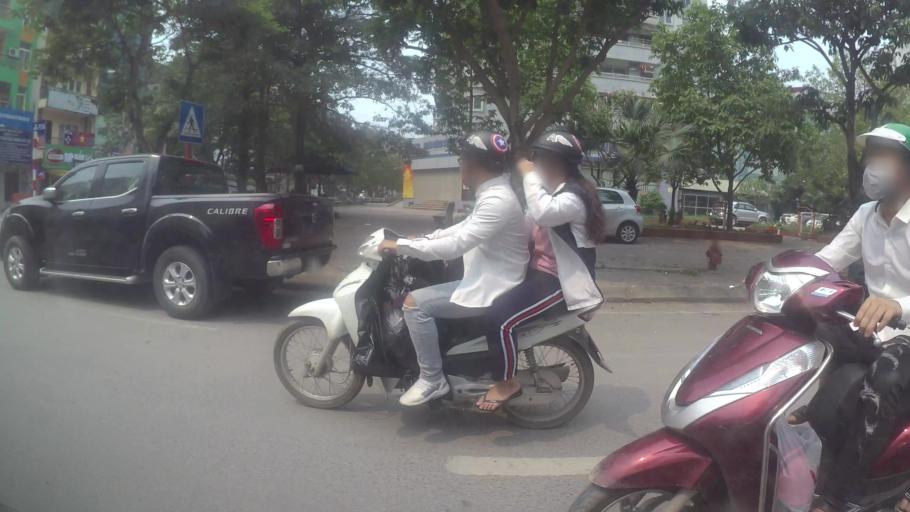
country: VN
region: Ha Noi
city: Cau Dien
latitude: 21.0352
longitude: 105.7640
